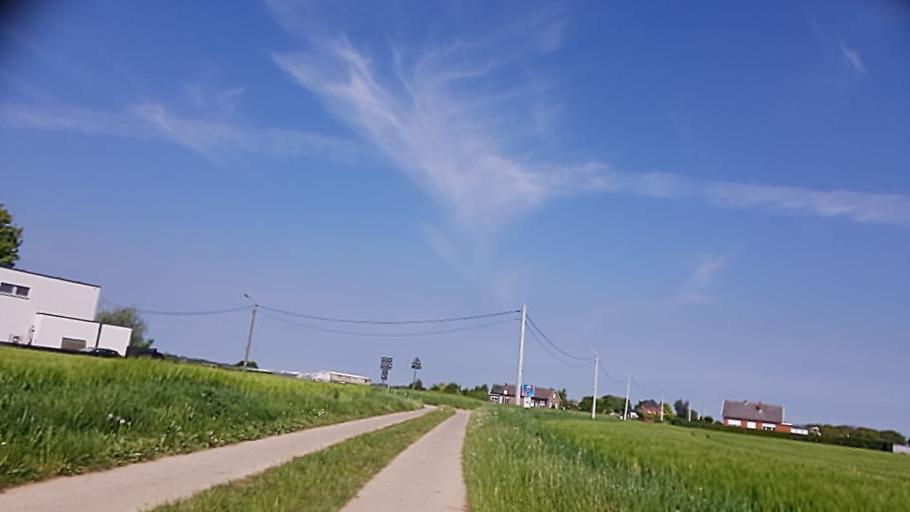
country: BE
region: Flanders
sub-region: Provincie Vlaams-Brabant
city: Huldenberg
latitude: 50.8032
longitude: 4.5657
